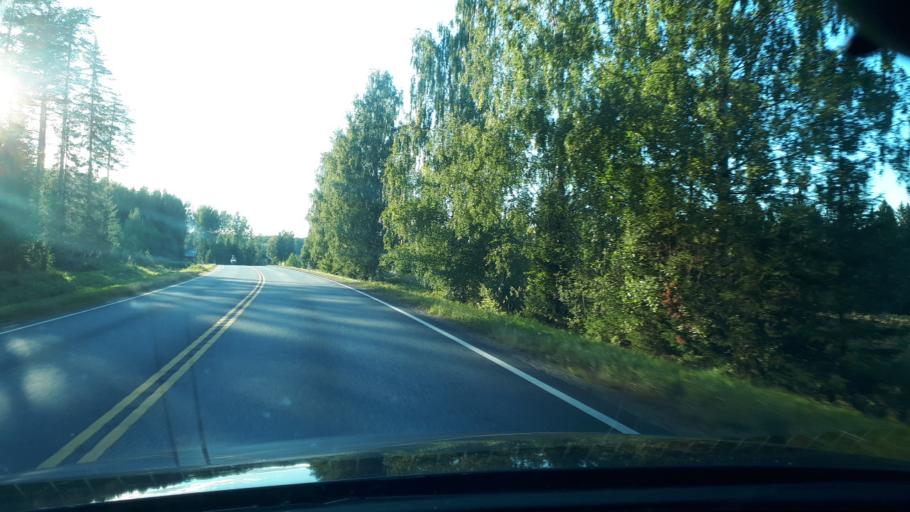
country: FI
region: Northern Savo
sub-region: Ylae-Savo
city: Vieremae
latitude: 63.6511
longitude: 27.0947
